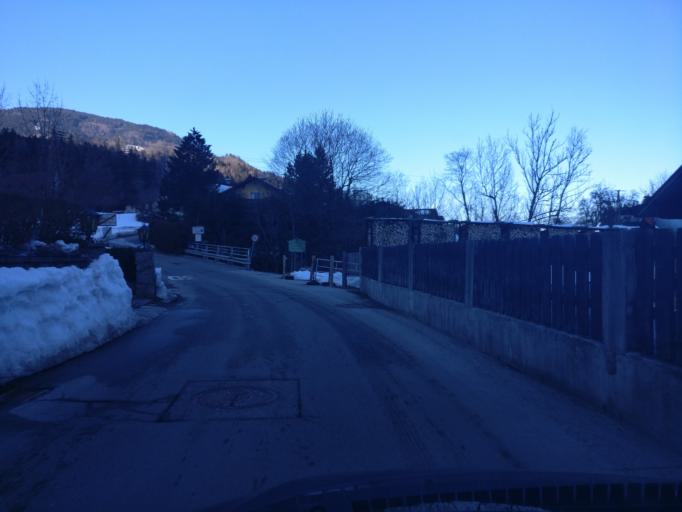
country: AT
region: Salzburg
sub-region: Politischer Bezirk Hallein
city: Golling an der Salzach
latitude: 47.6029
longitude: 13.1434
